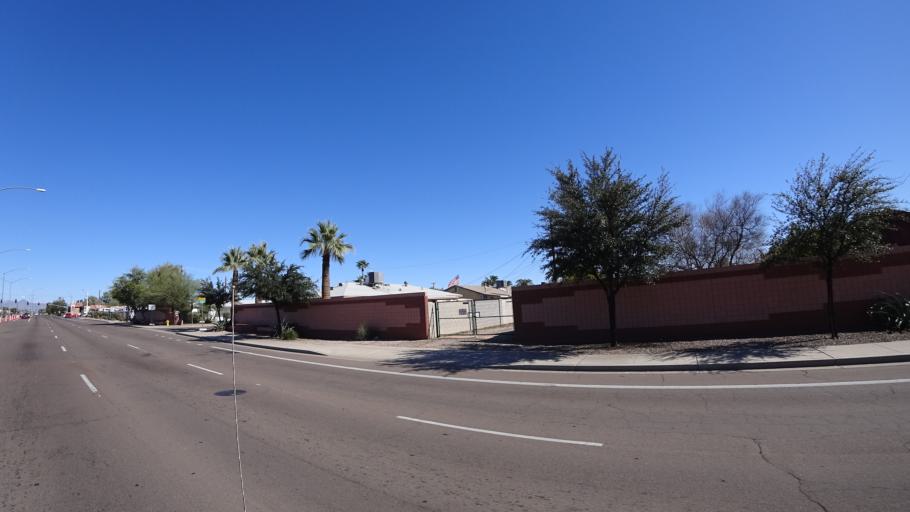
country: US
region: Arizona
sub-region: Maricopa County
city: Mesa
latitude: 33.4134
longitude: -111.7885
